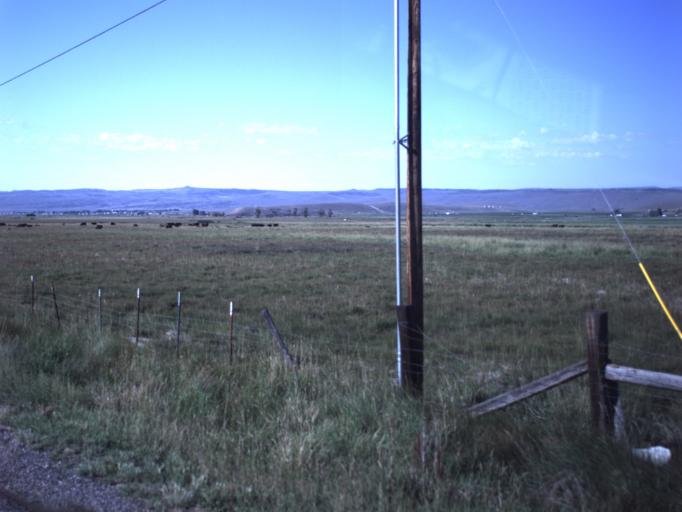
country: US
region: Utah
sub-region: Wayne County
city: Loa
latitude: 38.4548
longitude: -111.6158
